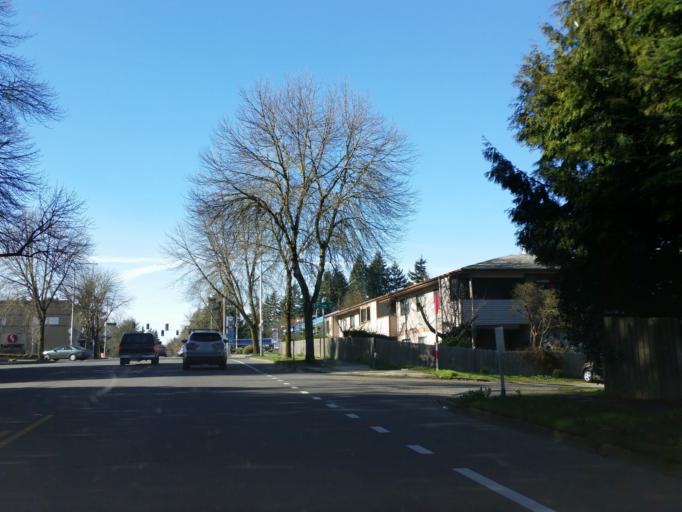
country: US
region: Washington
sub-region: King County
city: Shoreline
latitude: 47.7194
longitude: -122.3107
